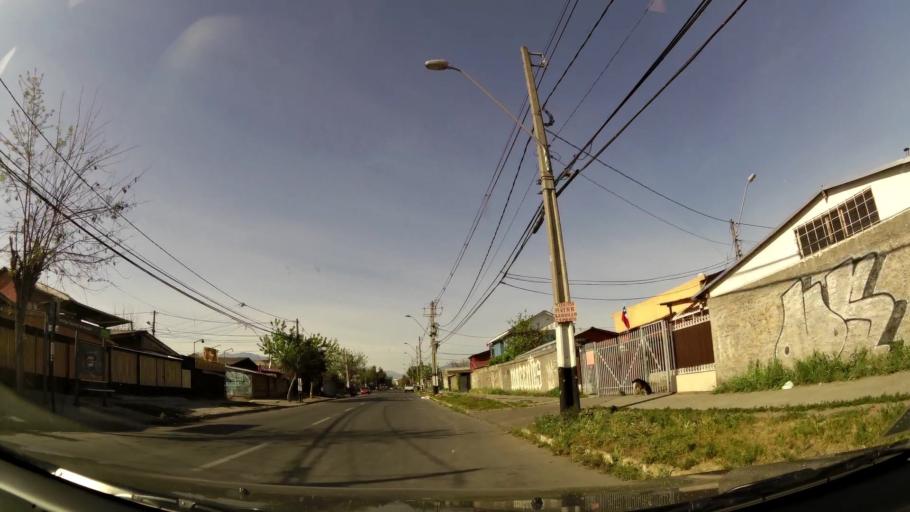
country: CL
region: Santiago Metropolitan
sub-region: Provincia de Cordillera
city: Puente Alto
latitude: -33.6063
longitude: -70.5973
